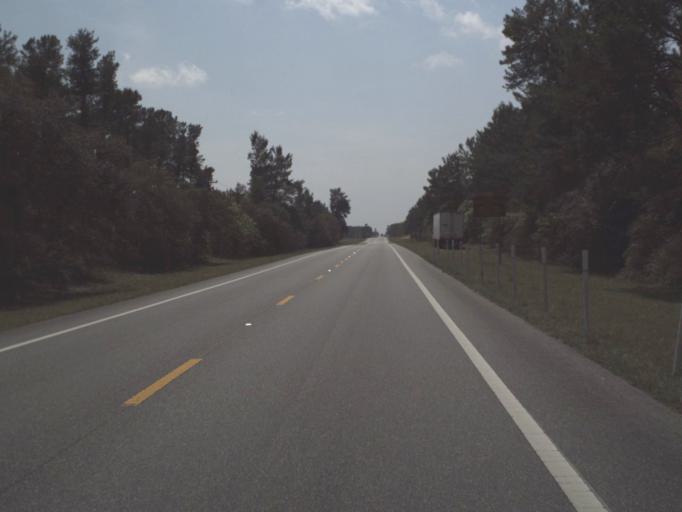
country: US
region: Florida
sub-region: Lake County
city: Astor
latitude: 29.1640
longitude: -81.6404
